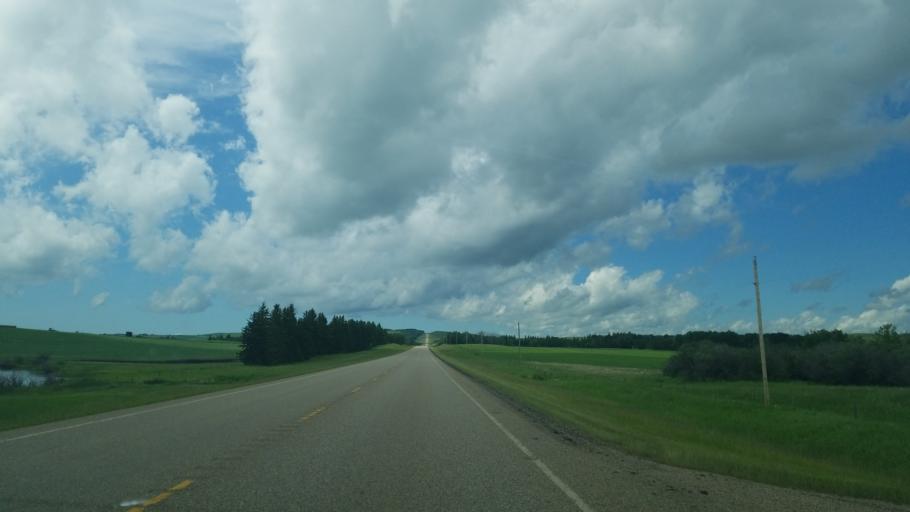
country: CA
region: Saskatchewan
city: Lloydminster
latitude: 53.1616
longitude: -110.1883
